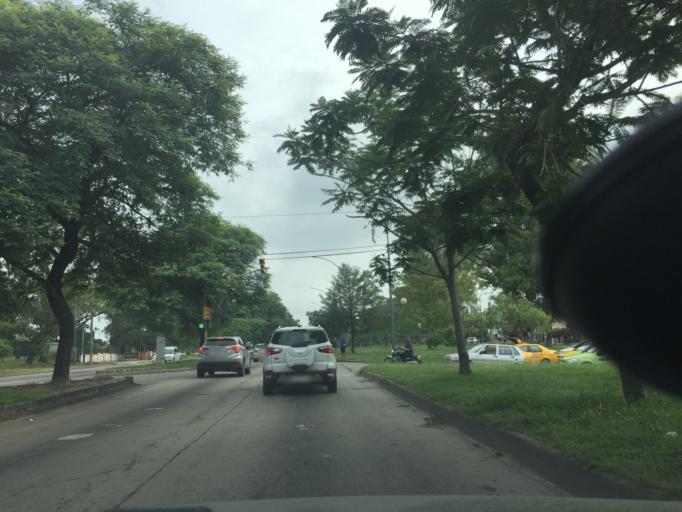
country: AR
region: Cordoba
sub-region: Departamento de Capital
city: Cordoba
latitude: -31.4380
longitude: -64.1960
